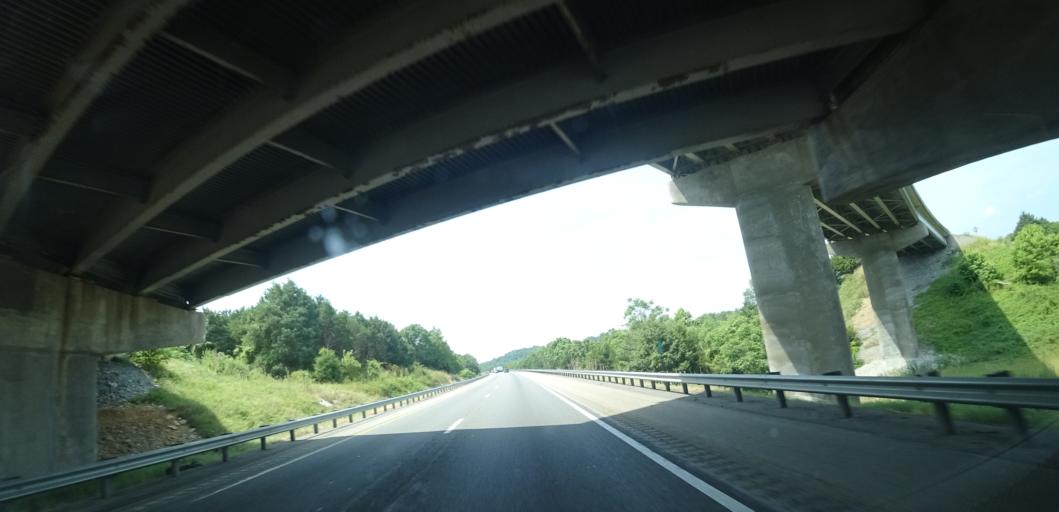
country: US
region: Virginia
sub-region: Rockbridge County
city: East Lexington
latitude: 37.7947
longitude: -79.3975
